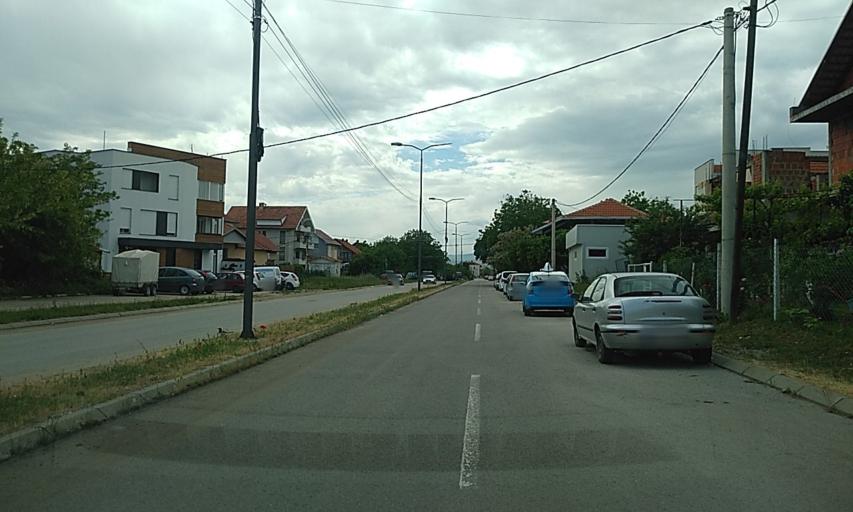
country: RS
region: Central Serbia
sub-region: Nisavski Okrug
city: Nis
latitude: 43.3347
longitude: 21.9076
